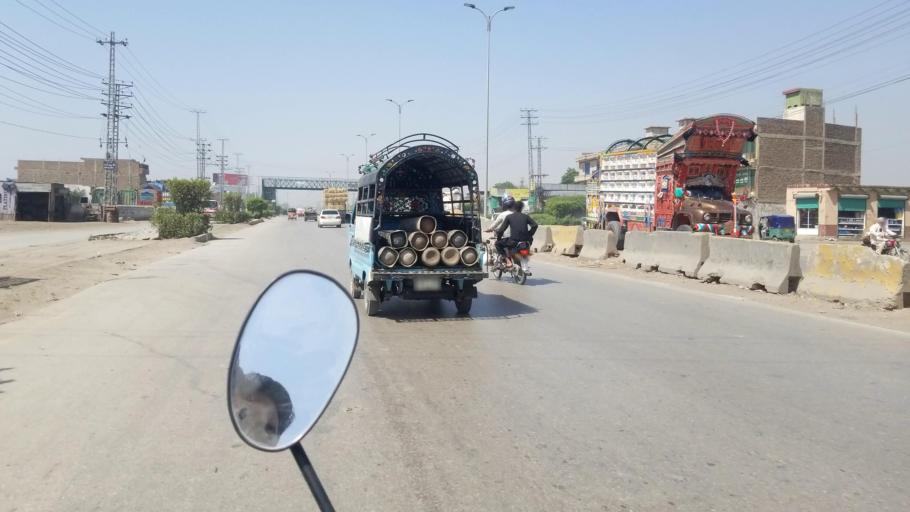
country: PK
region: Khyber Pakhtunkhwa
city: Peshawar
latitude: 33.9900
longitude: 71.5921
